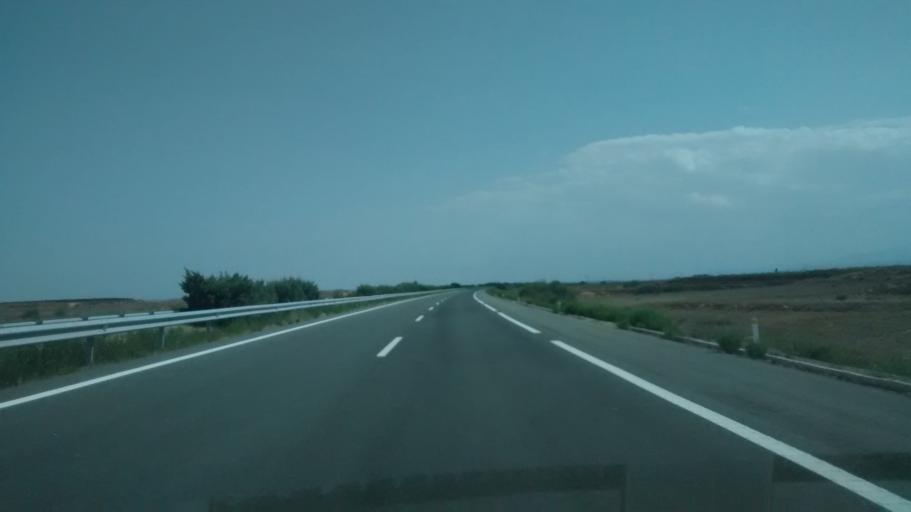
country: ES
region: La Rioja
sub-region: Provincia de La Rioja
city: Rincon de Soto
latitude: 42.1917
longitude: -1.8451
